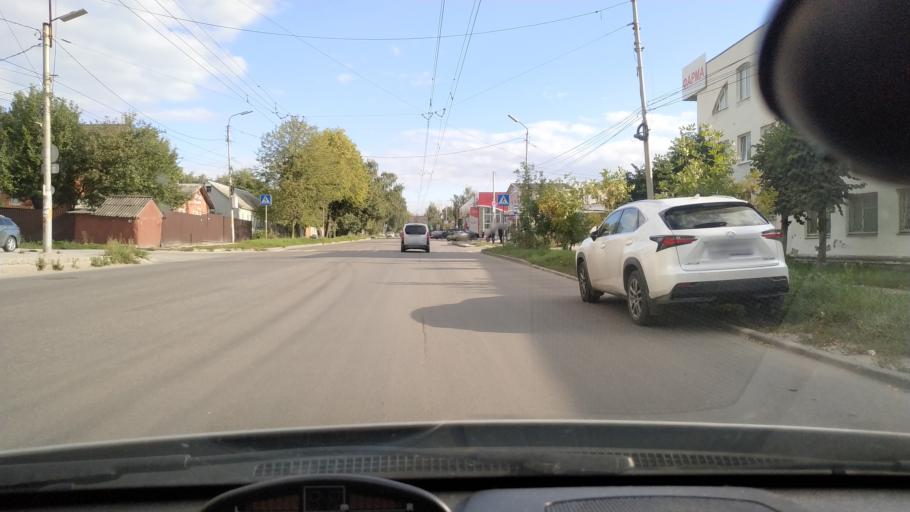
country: RU
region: Rjazan
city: Ryazan'
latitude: 54.6131
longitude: 39.6959
